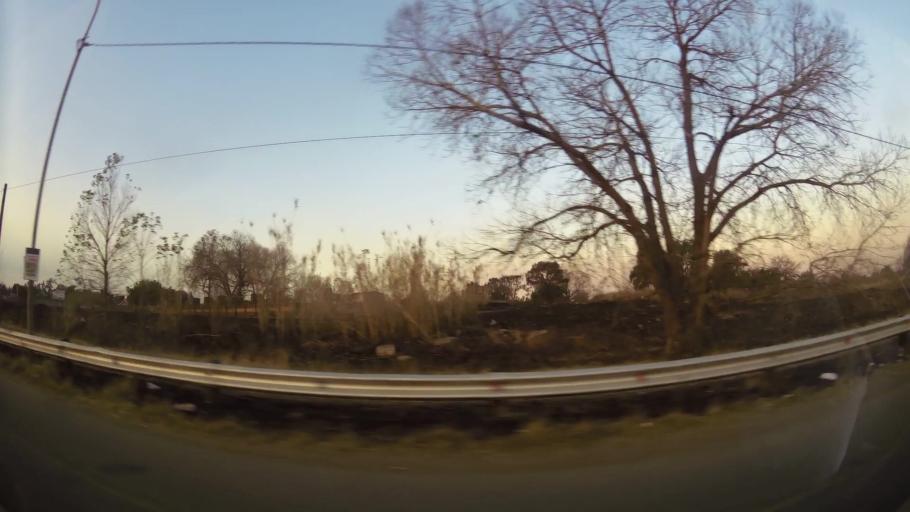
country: ZA
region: Gauteng
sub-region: Ekurhuleni Metropolitan Municipality
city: Springs
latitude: -26.2709
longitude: 28.4060
